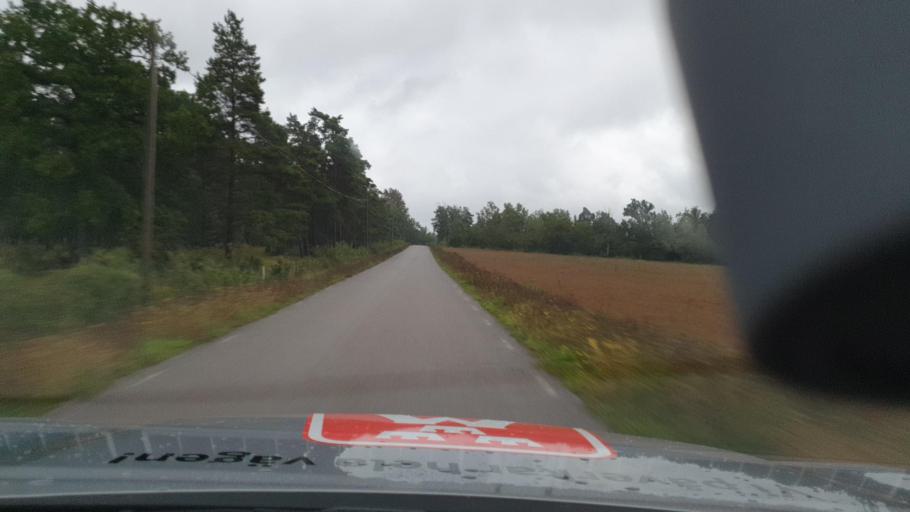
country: SE
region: Gotland
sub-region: Gotland
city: Slite
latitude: 57.7678
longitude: 18.6455
